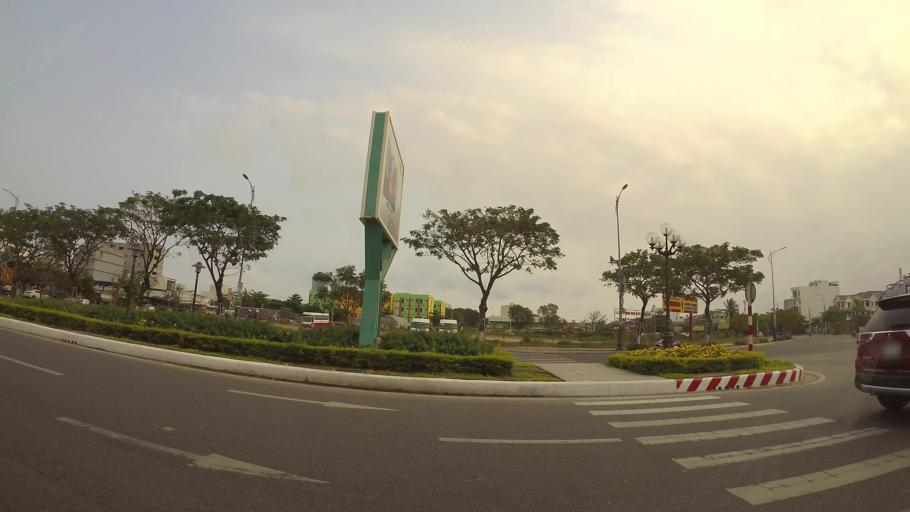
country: VN
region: Da Nang
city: Son Tra
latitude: 16.0627
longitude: 108.2406
